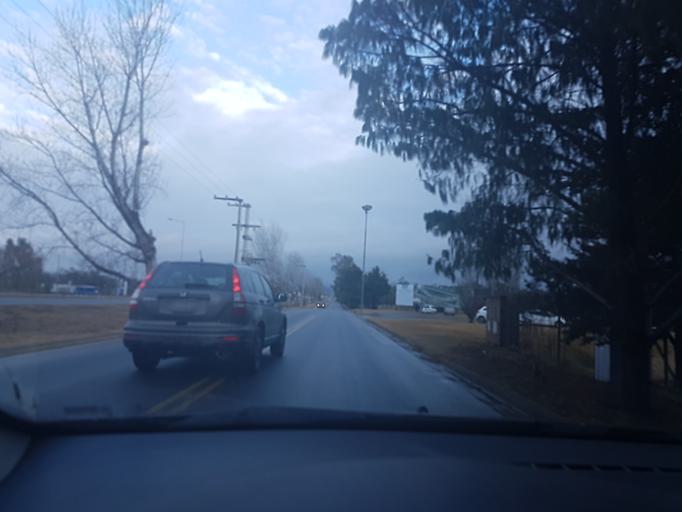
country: AR
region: Cordoba
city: Villa Allende
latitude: -31.3009
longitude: -64.2690
